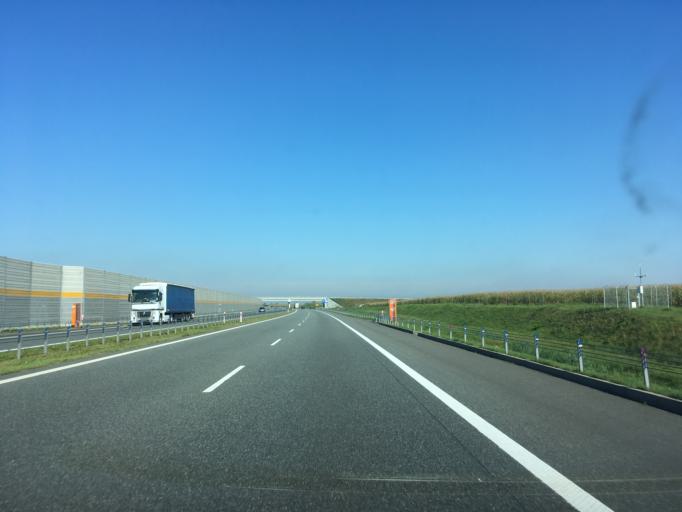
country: PL
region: Kujawsko-Pomorskie
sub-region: Powiat wabrzeski
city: Pluznica
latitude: 53.2087
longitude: 18.7397
